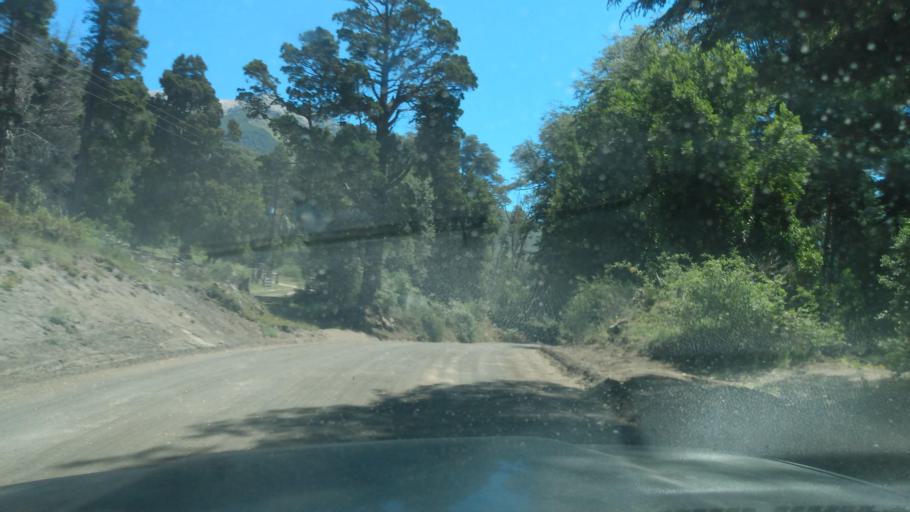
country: AR
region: Neuquen
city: Villa La Angostura
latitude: -40.6503
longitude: -71.4277
